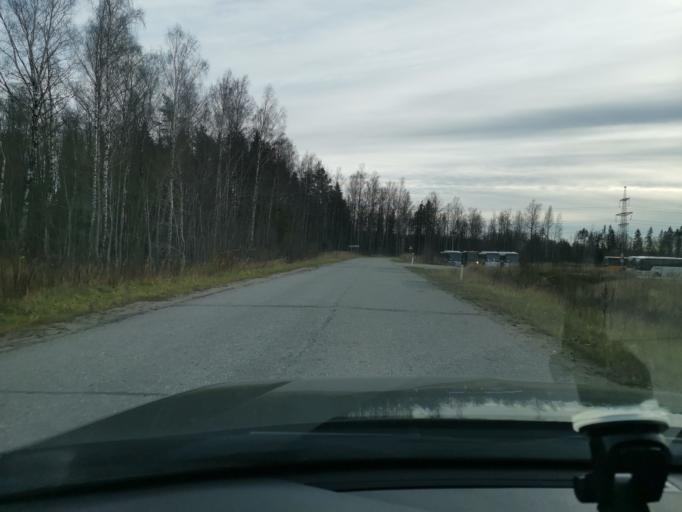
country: EE
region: Ida-Virumaa
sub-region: Sillamaee linn
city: Sillamae
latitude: 59.2716
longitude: 27.9130
